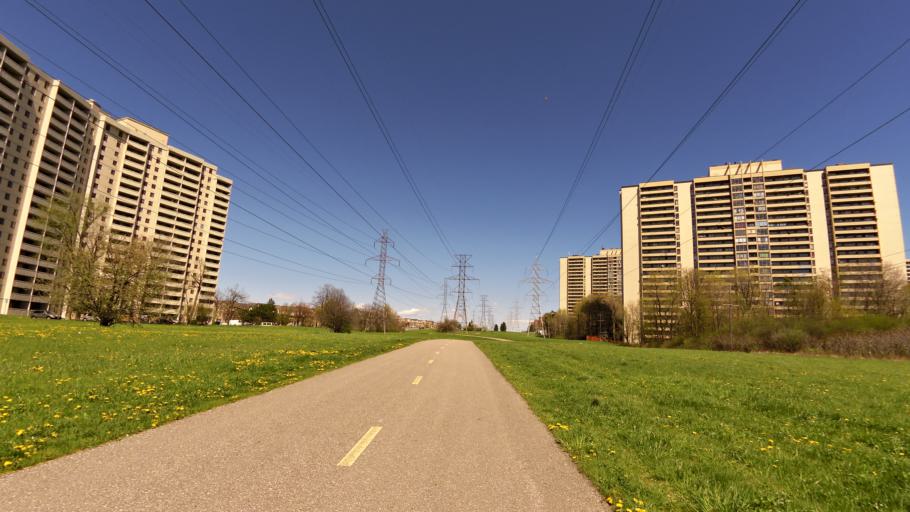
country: CA
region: Ontario
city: Concord
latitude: 43.7629
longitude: -79.5062
